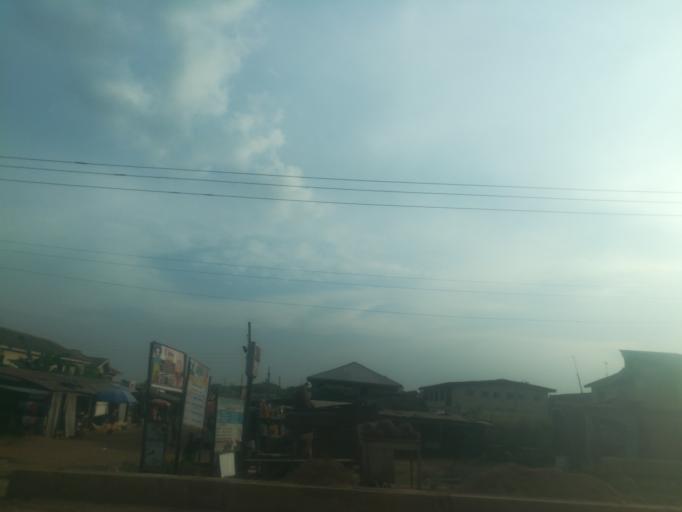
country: NG
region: Ogun
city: Abeokuta
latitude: 7.1661
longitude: 3.3051
